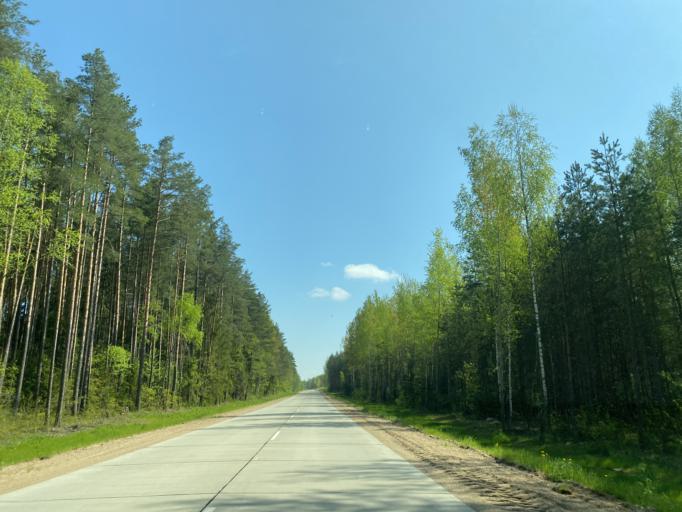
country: BY
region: Minsk
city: Horad Barysaw
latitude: 54.1742
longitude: 28.5287
